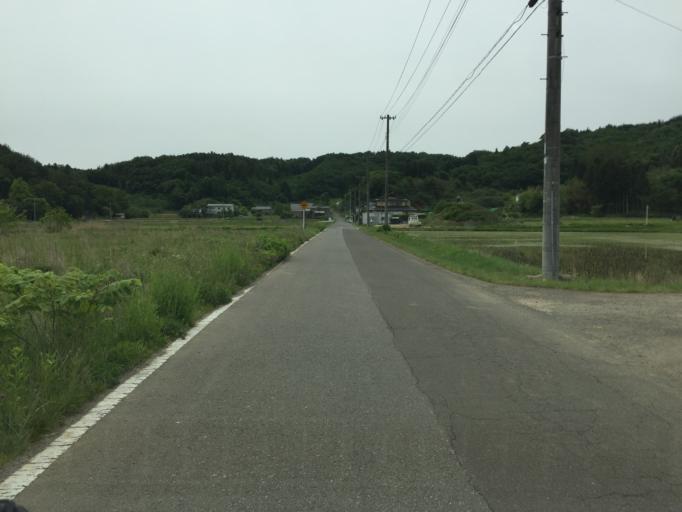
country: JP
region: Fukushima
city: Fukushima-shi
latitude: 37.7273
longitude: 140.4190
